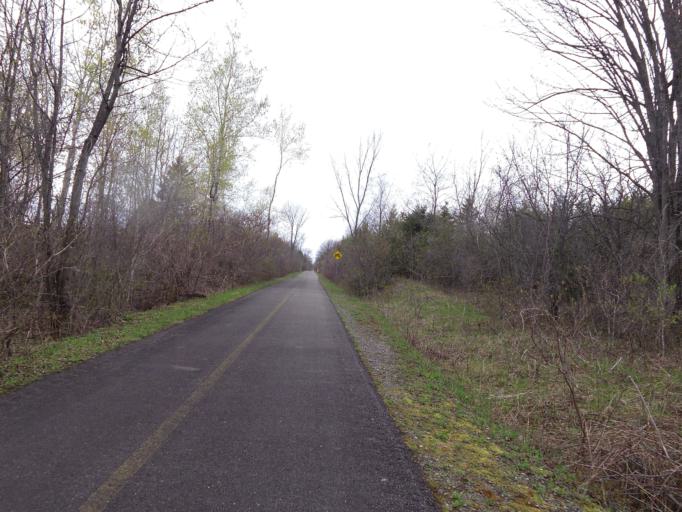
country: CA
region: Quebec
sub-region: Laurentides
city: Lachute
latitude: 45.5803
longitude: -74.4062
